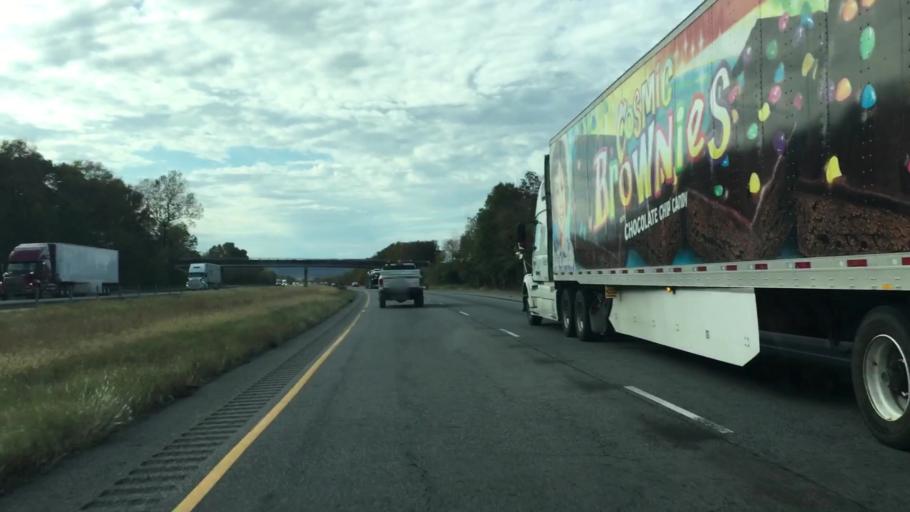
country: US
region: Arkansas
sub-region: Pope County
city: Atkins
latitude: 35.2472
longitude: -92.8698
